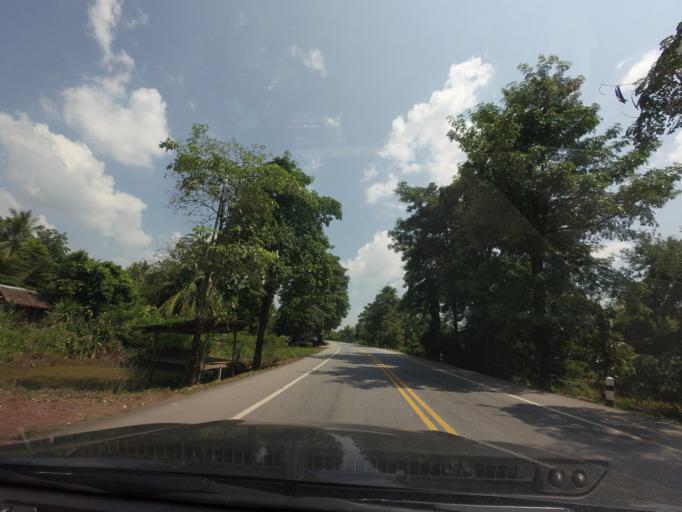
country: TH
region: Uttaradit
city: Thong Saen Khan
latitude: 17.2969
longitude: 100.4096
